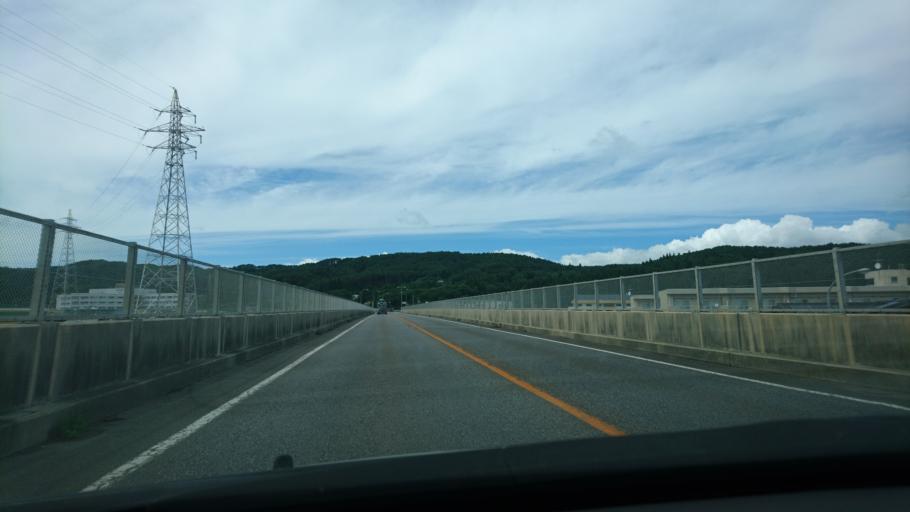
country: JP
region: Aomori
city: Hachinohe
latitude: 40.1970
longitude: 141.7824
